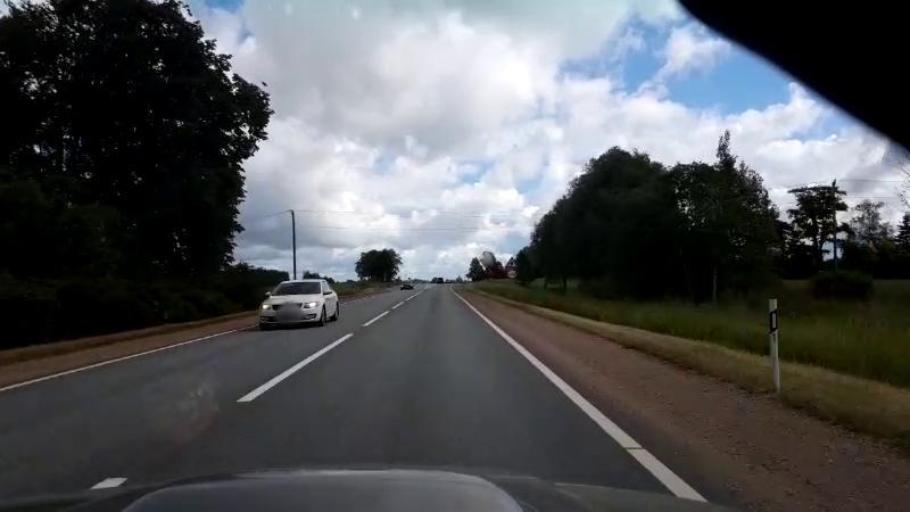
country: LV
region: Bauskas Rajons
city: Bauska
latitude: 56.4777
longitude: 24.1727
